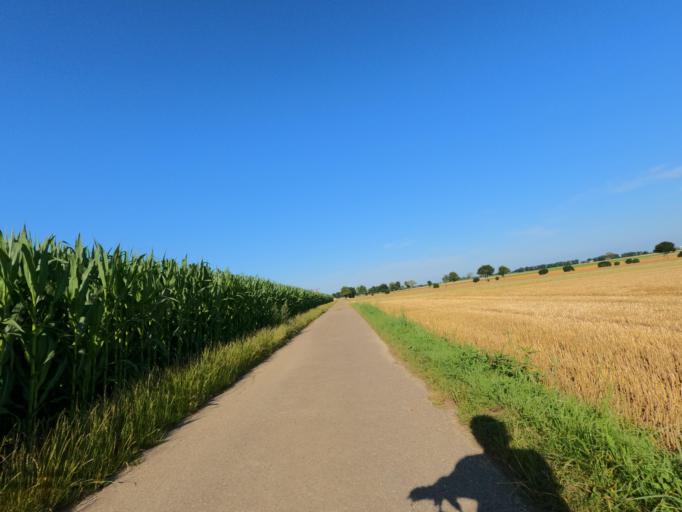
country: DE
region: North Rhine-Westphalia
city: Erkelenz
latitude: 51.0957
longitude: 6.3896
